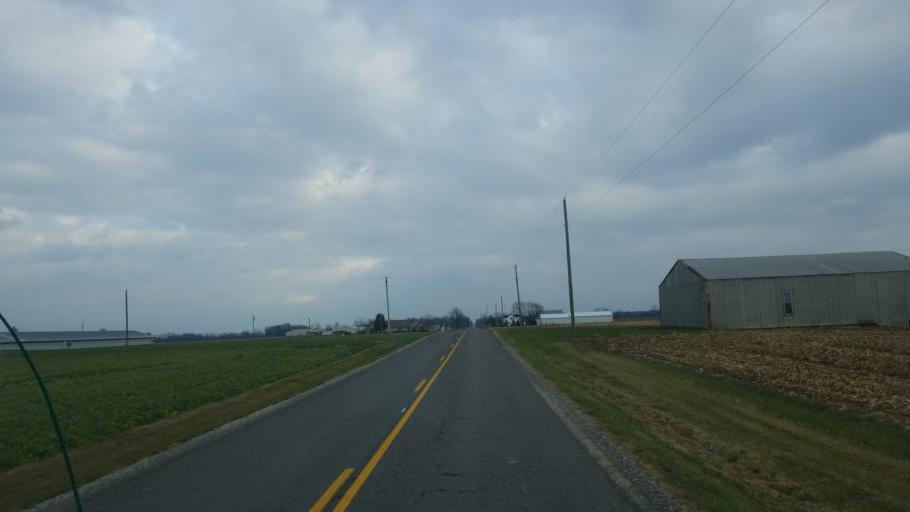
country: US
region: Ohio
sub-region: Mercer County
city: Coldwater
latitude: 40.5089
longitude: -84.6701
